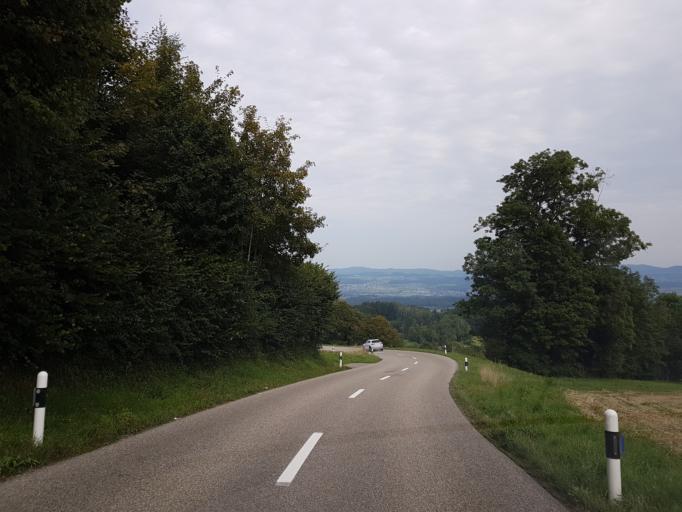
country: CH
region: Aargau
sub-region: Bezirk Muri
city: Buttwil
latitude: 47.2745
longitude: 8.2989
